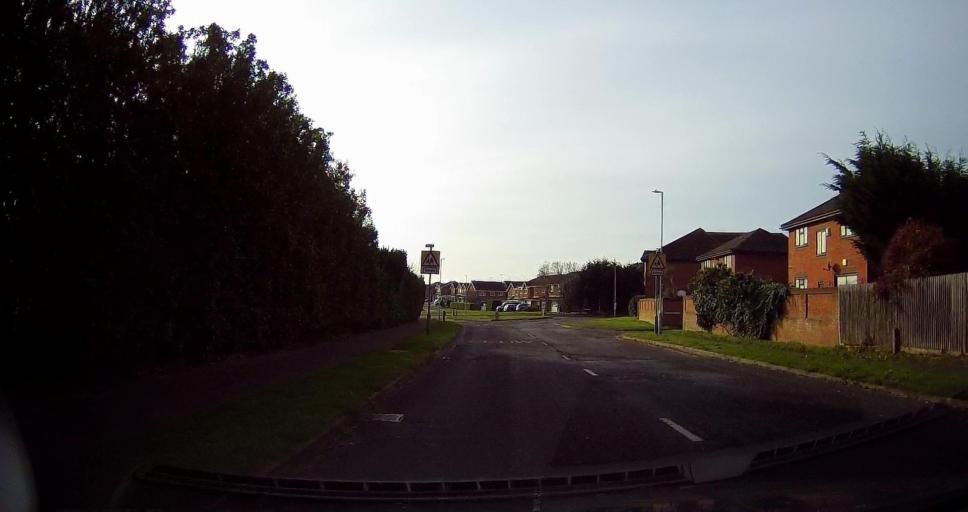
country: GB
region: England
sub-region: East Sussex
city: Peacehaven
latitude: 50.8046
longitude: -0.0044
